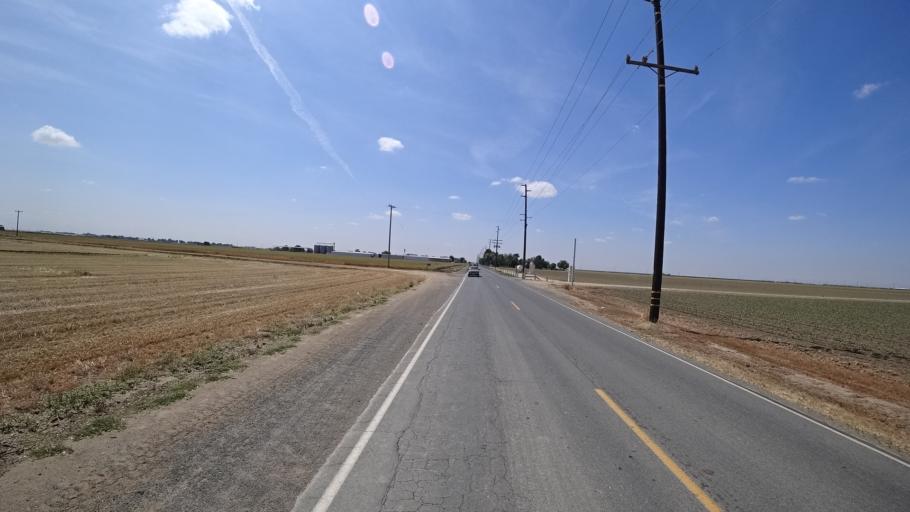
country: US
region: California
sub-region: Tulare County
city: Goshen
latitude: 36.3059
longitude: -119.4927
